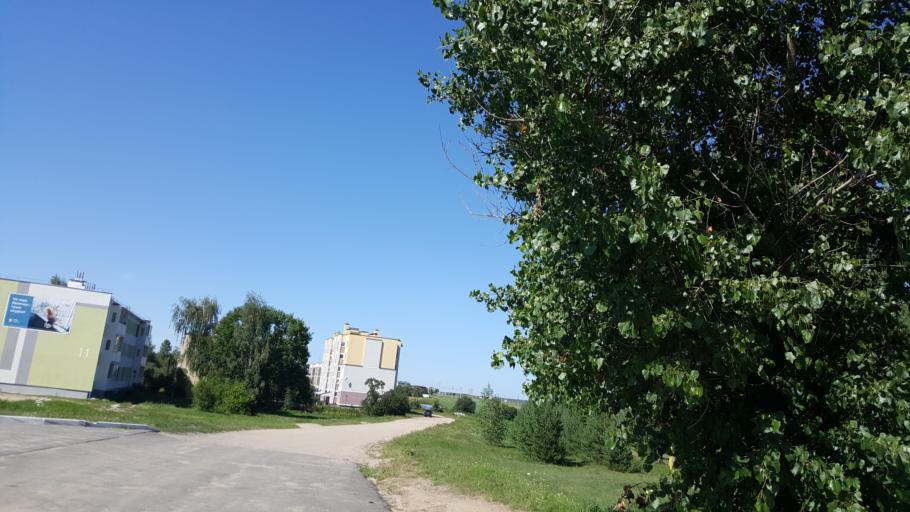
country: BY
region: Brest
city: Charnawchytsy
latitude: 52.2121
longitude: 23.7460
